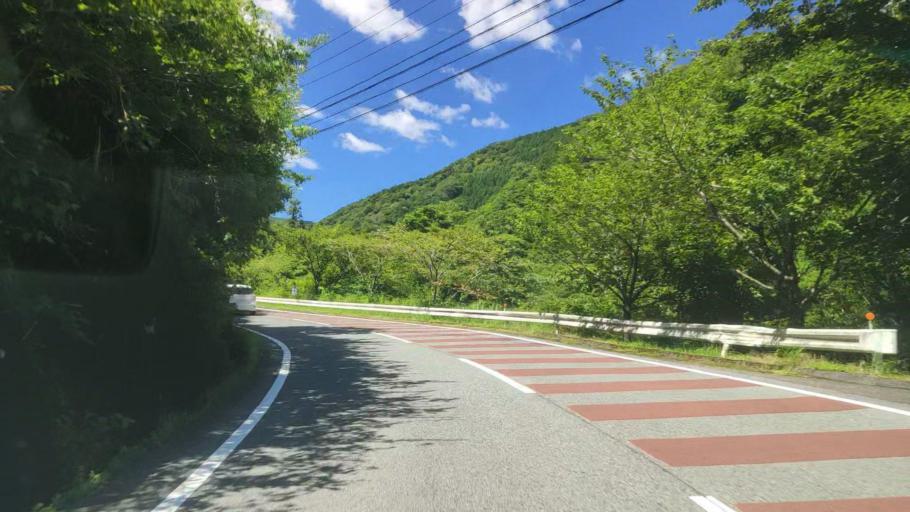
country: JP
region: Mie
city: Owase
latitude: 34.1974
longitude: 135.9998
